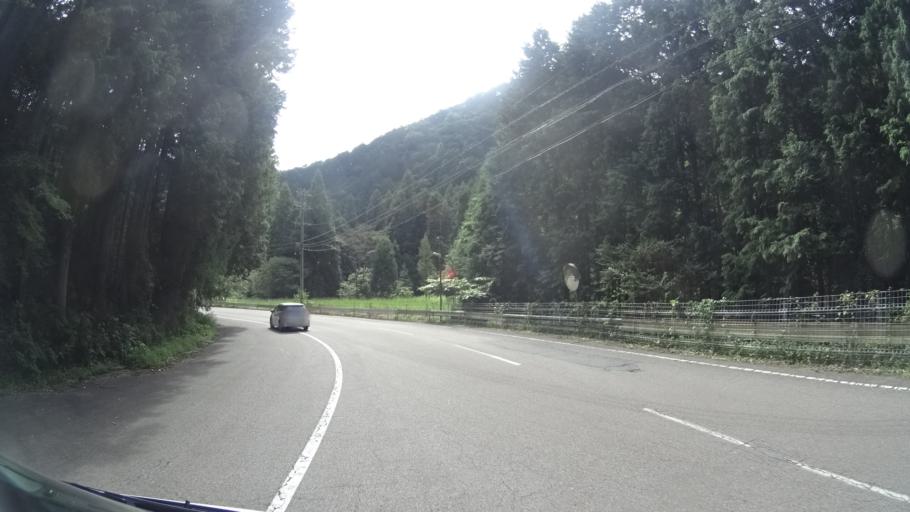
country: JP
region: Gifu
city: Minokamo
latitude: 35.5611
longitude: 137.0917
